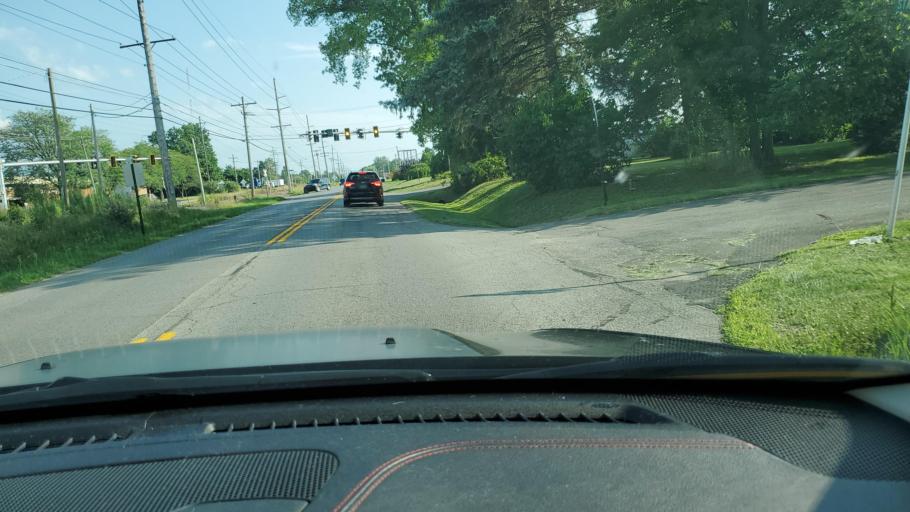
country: US
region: Ohio
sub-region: Mahoning County
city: Boardman
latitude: 41.0087
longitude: -80.6534
